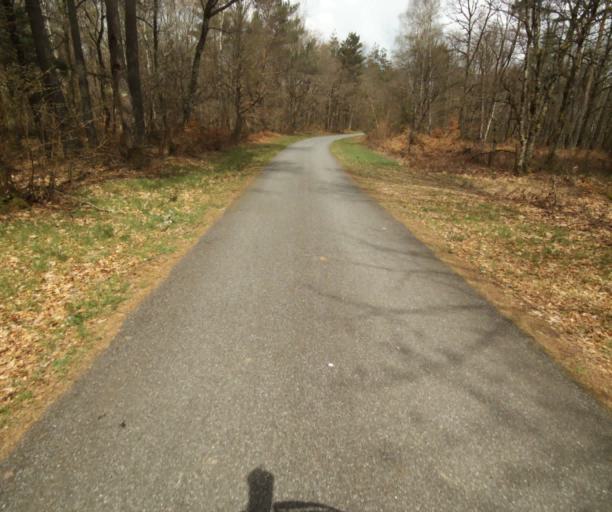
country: FR
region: Limousin
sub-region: Departement de la Correze
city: Correze
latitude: 45.3233
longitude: 1.8948
